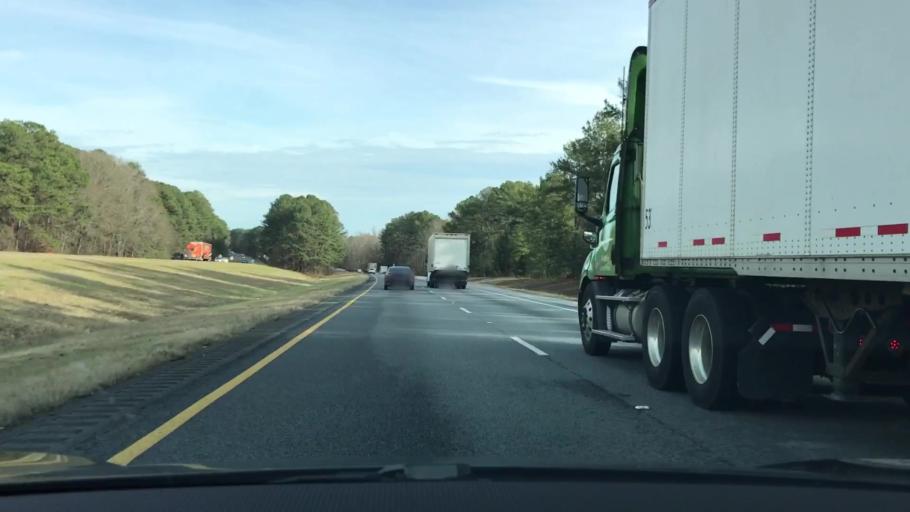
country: US
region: Georgia
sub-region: Morgan County
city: Madison
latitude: 33.5771
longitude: -83.5736
